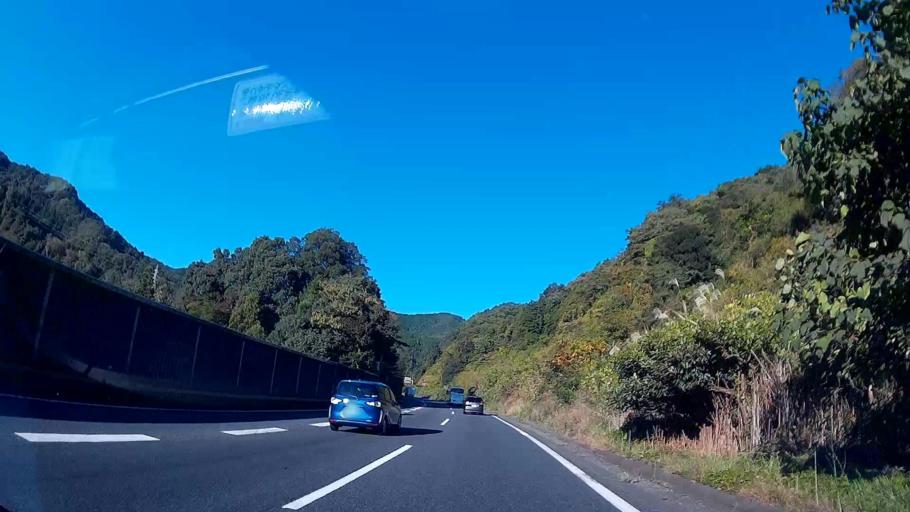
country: JP
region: Tokyo
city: Itsukaichi
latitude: 35.6404
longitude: 139.2357
